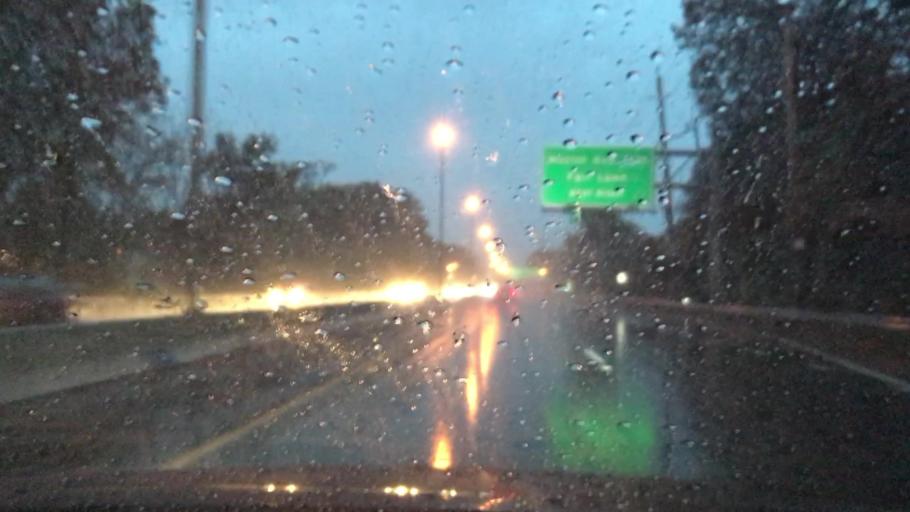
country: US
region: New Jersey
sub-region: Bergen County
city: Fair Lawn
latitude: 40.9306
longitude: -74.1073
